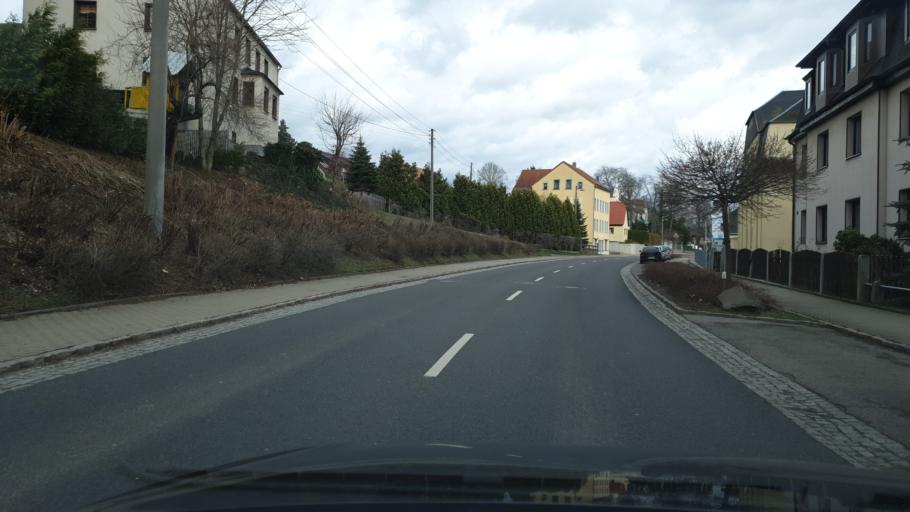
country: DE
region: Saxony
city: Taura
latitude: 50.9281
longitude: 12.8583
